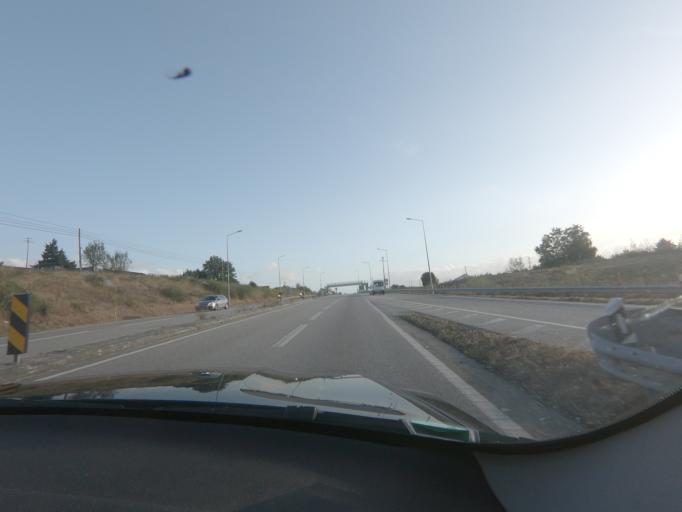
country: PT
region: Viseu
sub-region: Santa Comba Dao
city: Santa Comba Dao
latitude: 40.3792
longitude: -8.1188
